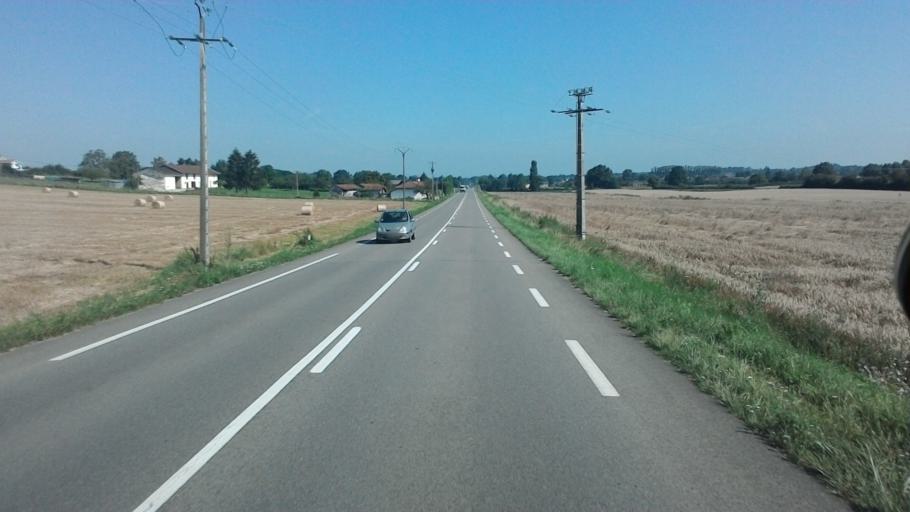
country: FR
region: Rhone-Alpes
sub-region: Departement de l'Ain
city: Montrevel-en-Bresse
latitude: 46.3817
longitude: 5.1169
